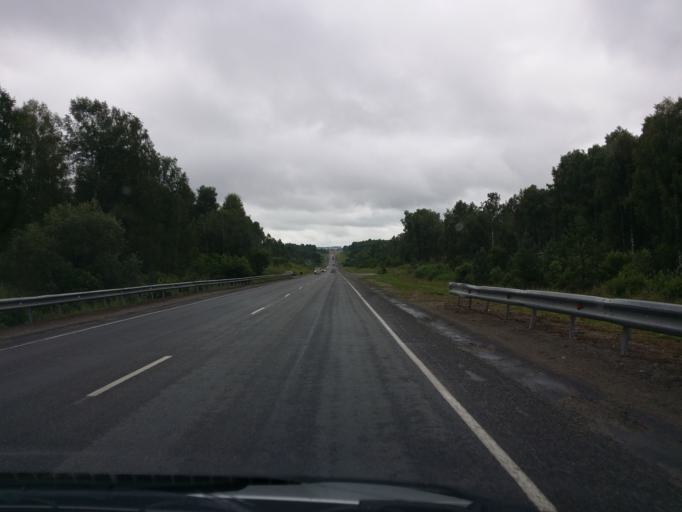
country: RU
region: Altai Krai
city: Troitskoye
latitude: 53.0100
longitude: 84.7226
